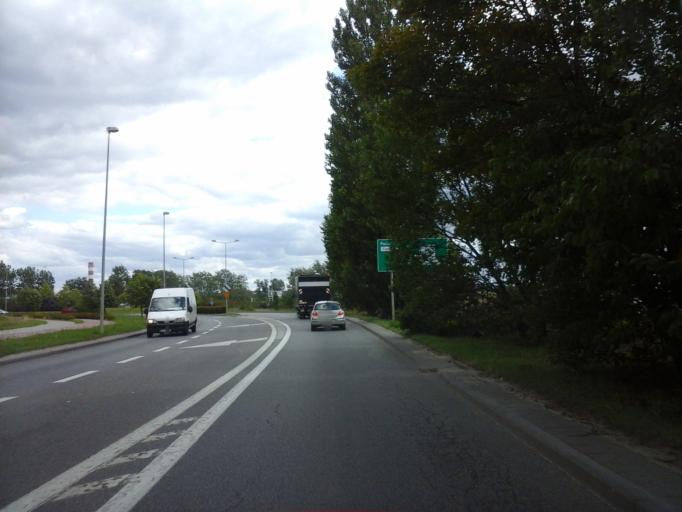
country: PL
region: West Pomeranian Voivodeship
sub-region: Powiat policki
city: Przeclaw
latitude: 53.3919
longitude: 14.4989
